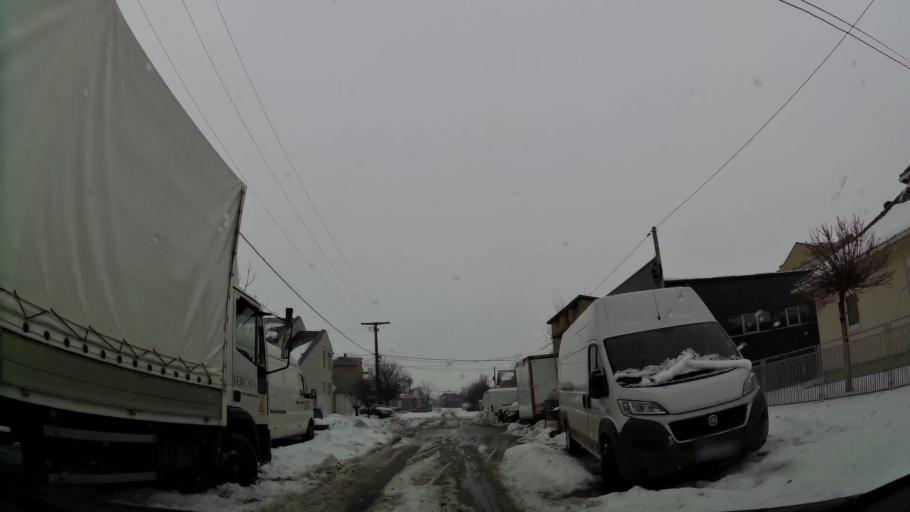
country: RS
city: Novi Banovci
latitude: 44.8766
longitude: 20.3125
